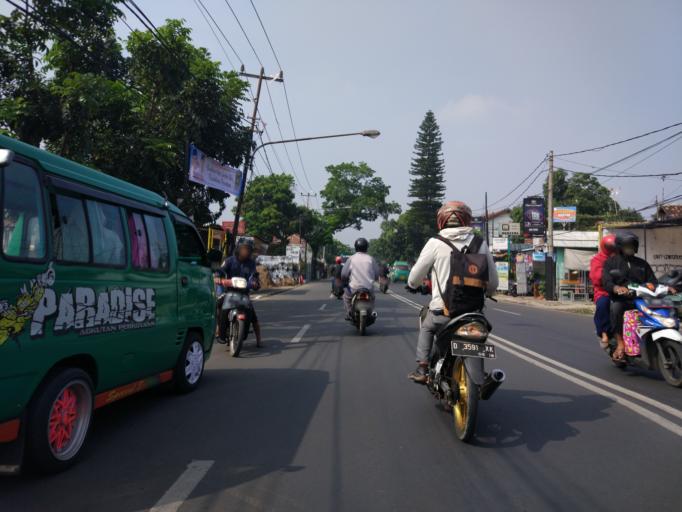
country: ID
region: West Java
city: Cileunyi
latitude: -6.9220
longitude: 107.7098
